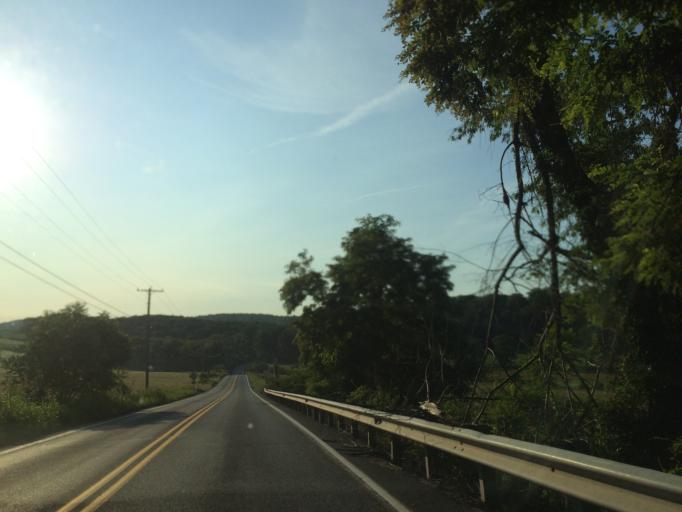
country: US
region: Pennsylvania
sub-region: York County
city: Glen Rock
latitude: 39.7492
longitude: -76.8036
